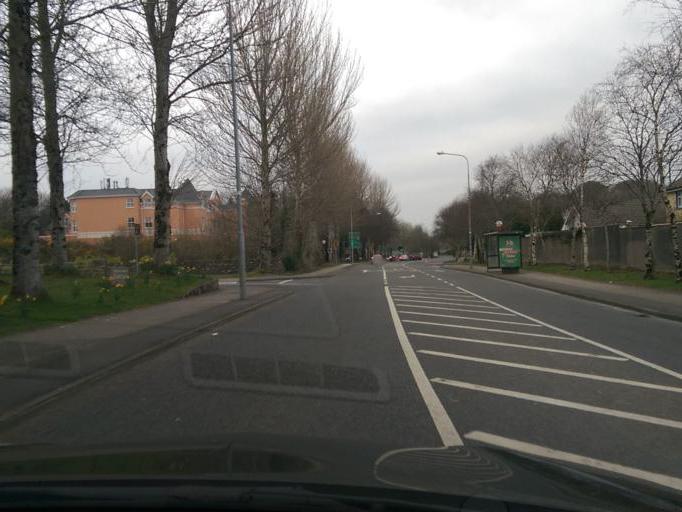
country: IE
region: Connaught
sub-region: County Galway
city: Gaillimh
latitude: 53.2879
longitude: -9.0749
